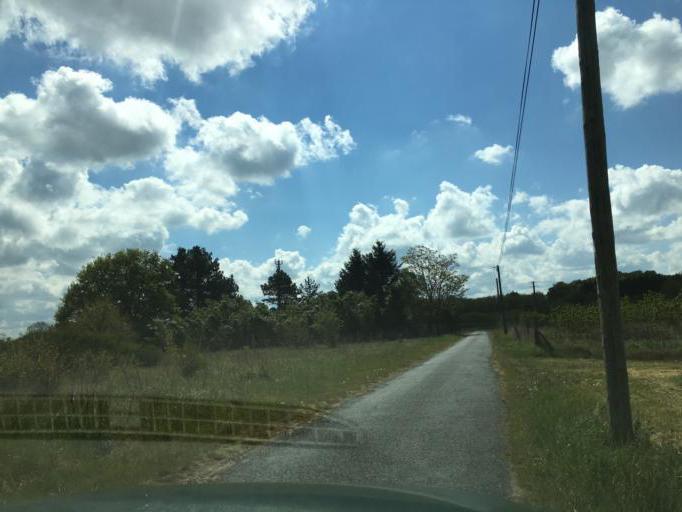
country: FR
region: Centre
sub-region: Departement du Loiret
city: Saint-Pryve-Saint-Mesmin
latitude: 47.8614
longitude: 1.8605
